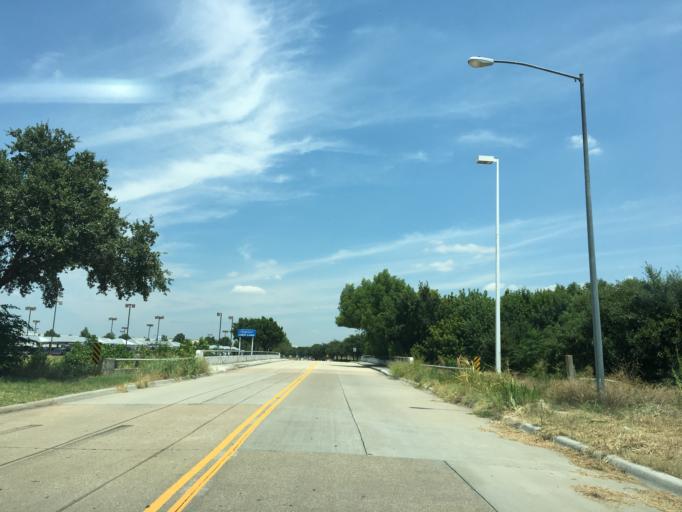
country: US
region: Texas
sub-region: Denton County
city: Lewisville
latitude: 33.0096
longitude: -96.9749
